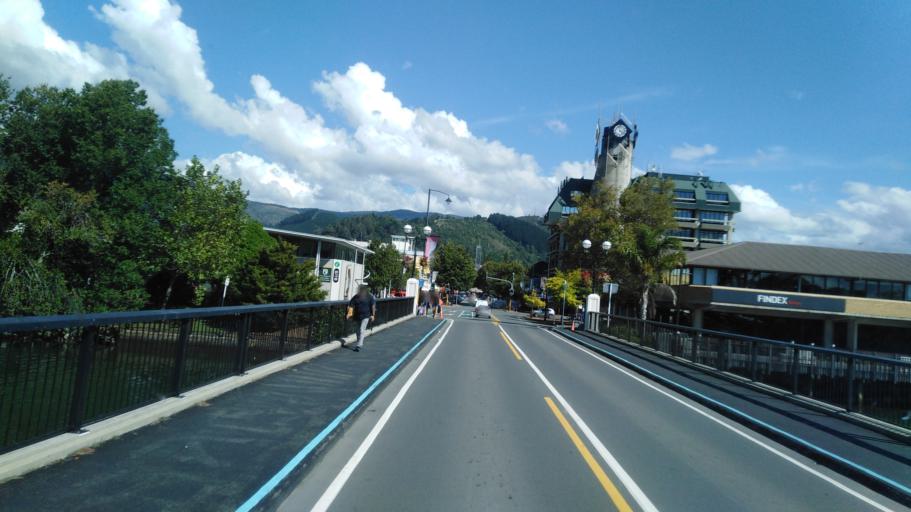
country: NZ
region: Nelson
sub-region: Nelson City
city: Nelson
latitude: -41.2697
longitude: 173.2841
